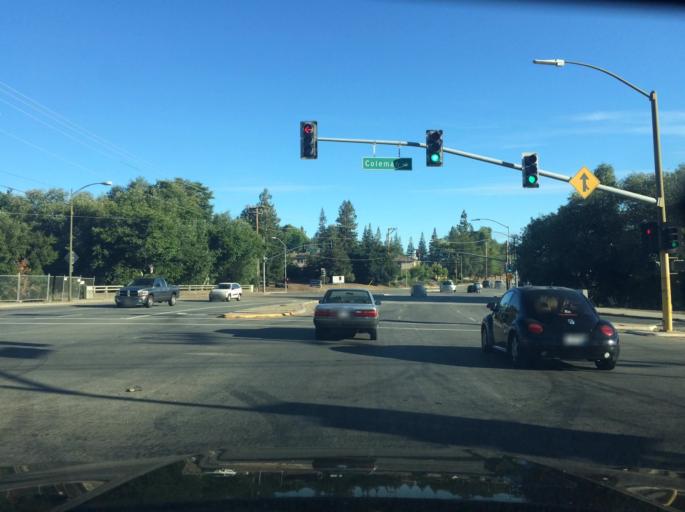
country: US
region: California
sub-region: Santa Clara County
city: Cambrian Park
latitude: 37.2258
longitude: -121.9034
